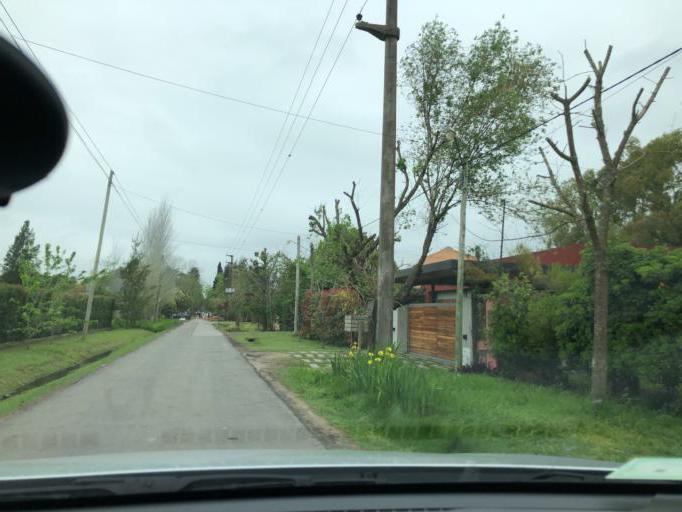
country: AR
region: Buenos Aires
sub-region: Partido de La Plata
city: La Plata
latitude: -34.8699
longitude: -58.0837
